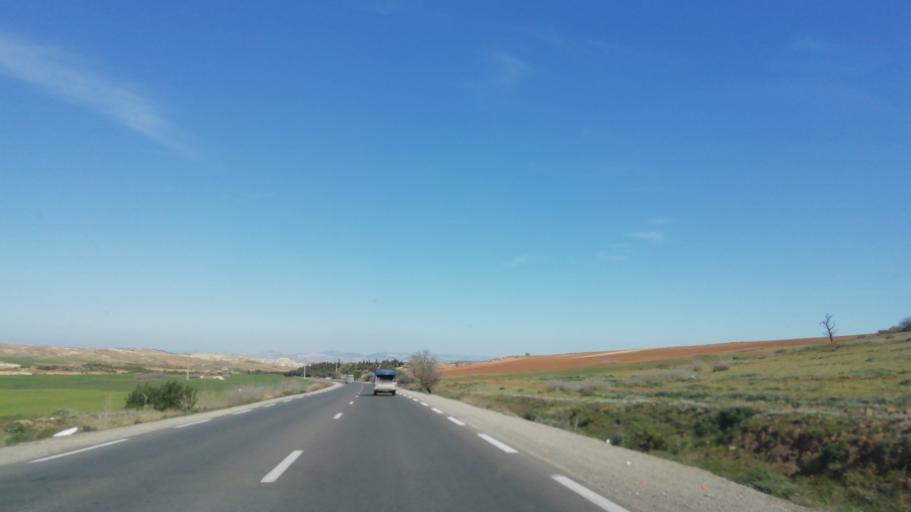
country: DZ
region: Mascara
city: Oued el Abtal
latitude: 35.4321
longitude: 0.4881
